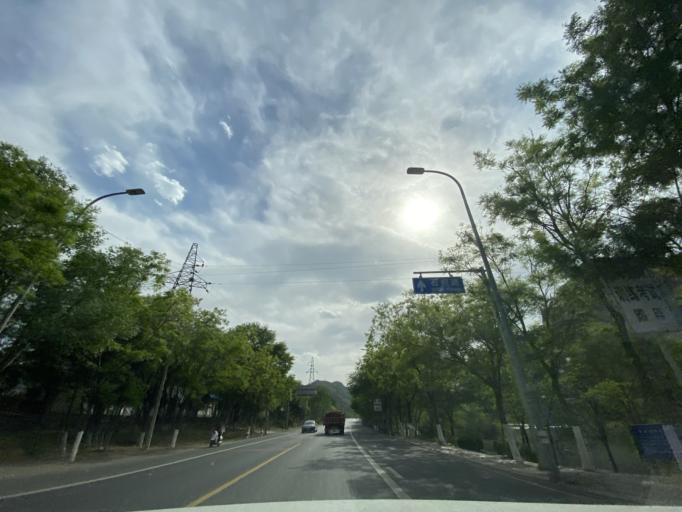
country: CN
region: Beijing
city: Miaofengshan
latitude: 39.9883
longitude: 116.0650
